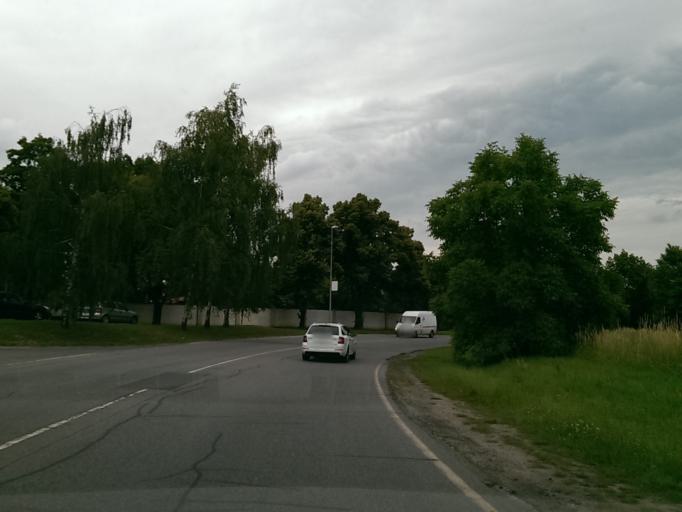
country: CZ
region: Central Bohemia
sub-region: Okres Praha-Zapad
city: Pruhonice
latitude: 50.0353
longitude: 14.5649
